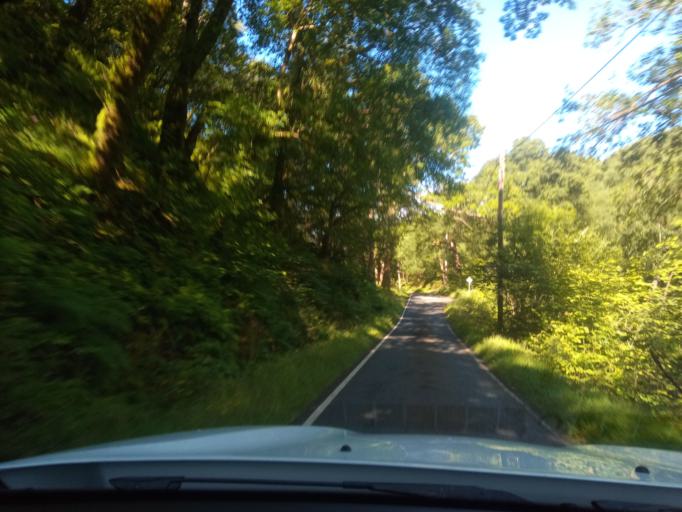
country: GB
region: Scotland
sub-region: Argyll and Bute
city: Isle Of Mull
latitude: 56.6928
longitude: -5.6706
